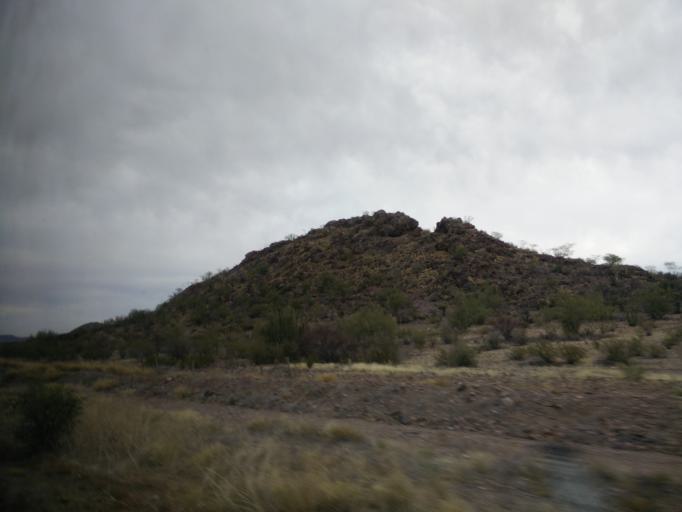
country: MX
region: Sonora
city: Hermosillo
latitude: 28.8353
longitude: -110.9582
